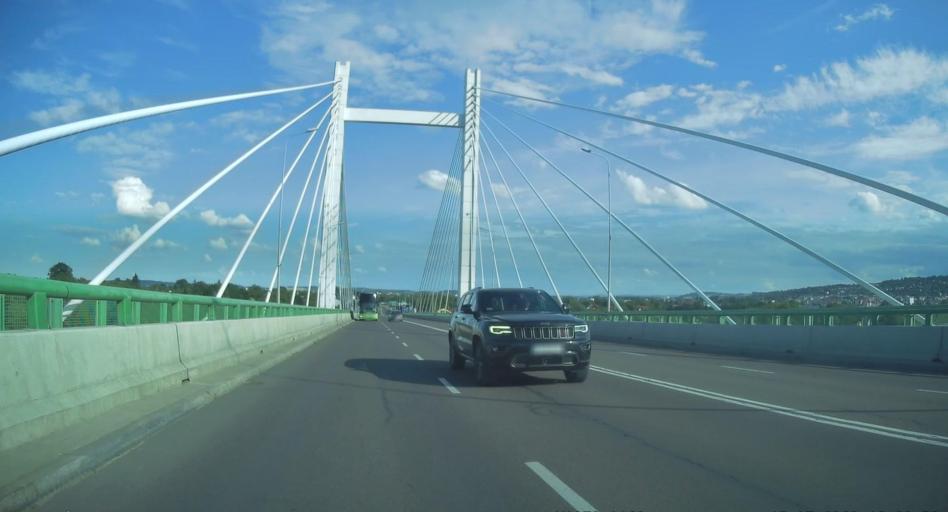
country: PL
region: Subcarpathian Voivodeship
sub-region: Przemysl
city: Przemysl
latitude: 49.7976
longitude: 22.7849
